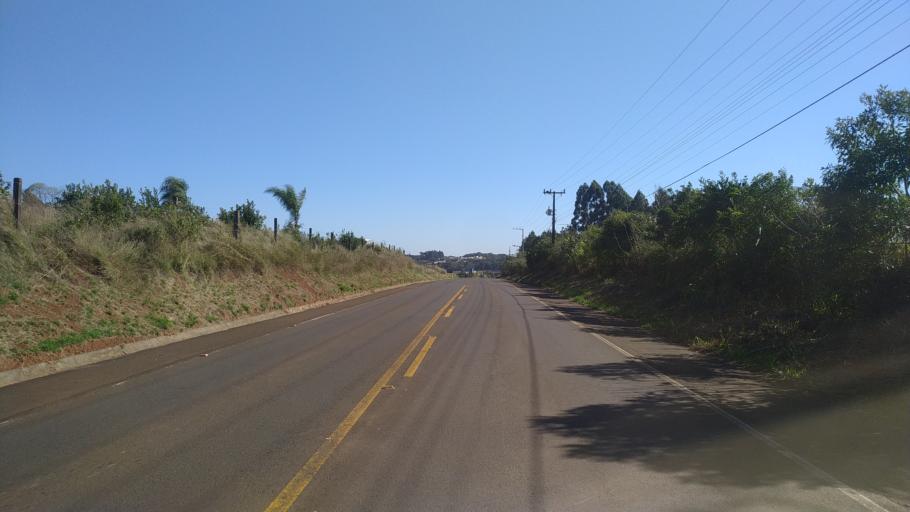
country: BR
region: Santa Catarina
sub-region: Chapeco
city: Chapeco
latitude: -27.1537
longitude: -52.6171
